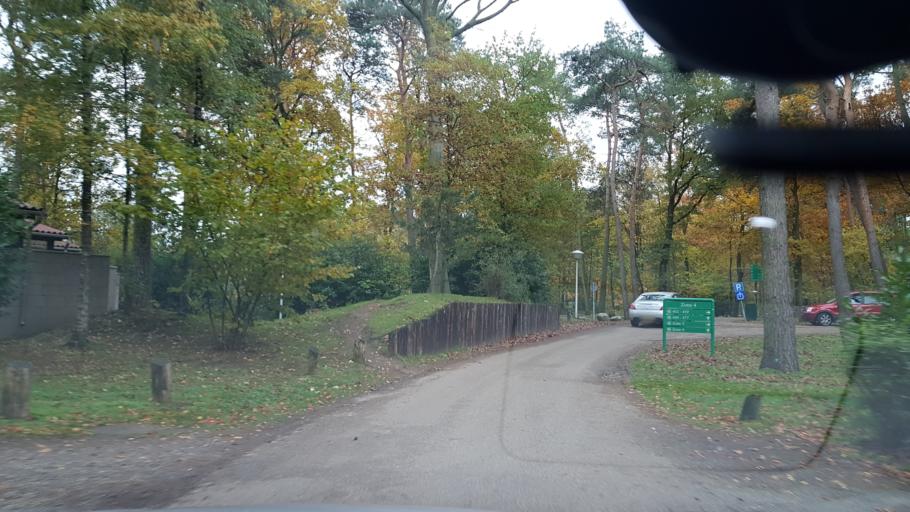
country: NL
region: Limburg
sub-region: Gemeente Beesel
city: Beesel
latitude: 51.2806
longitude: 6.0517
